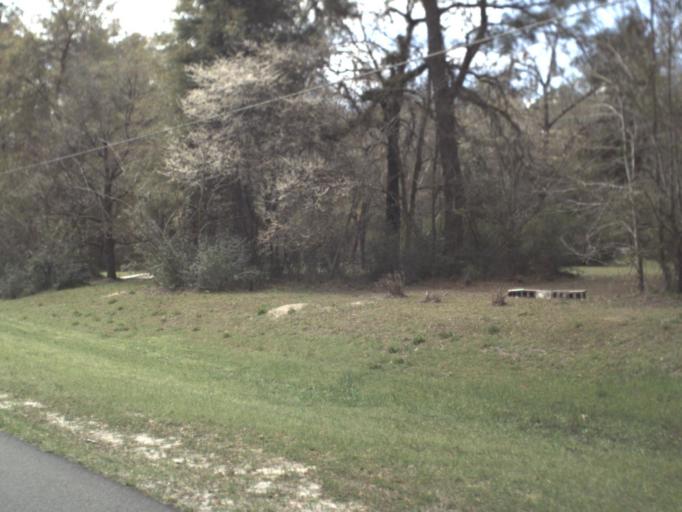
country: US
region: Florida
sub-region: Wakulla County
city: Crawfordville
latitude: 30.2731
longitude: -84.3593
